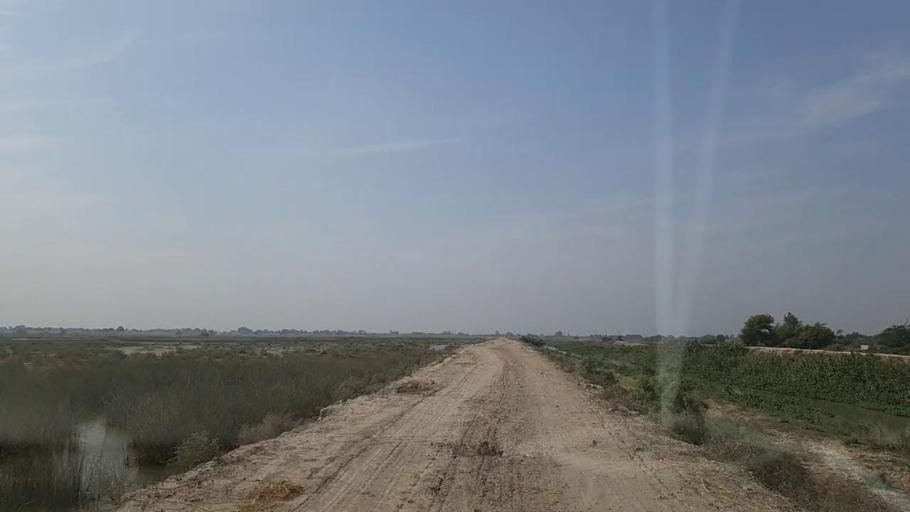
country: PK
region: Sindh
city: Mirpur Batoro
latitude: 24.6494
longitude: 68.2329
